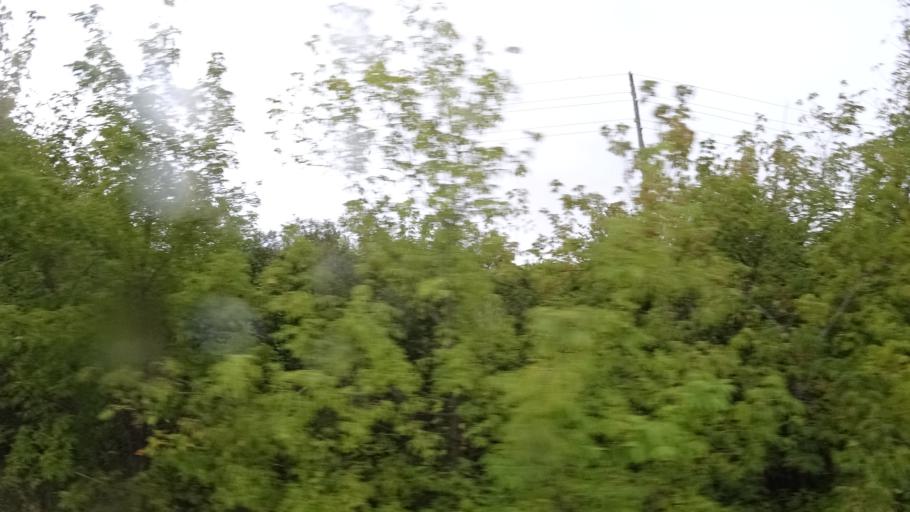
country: RU
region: Primorskiy
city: Chernigovka
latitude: 44.4055
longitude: 132.5319
